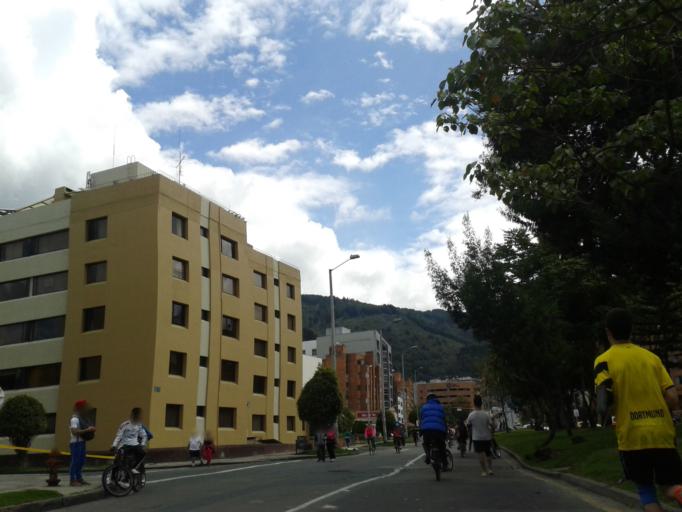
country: CO
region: Bogota D.C.
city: Barrio San Luis
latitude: 4.6953
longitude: -74.0381
